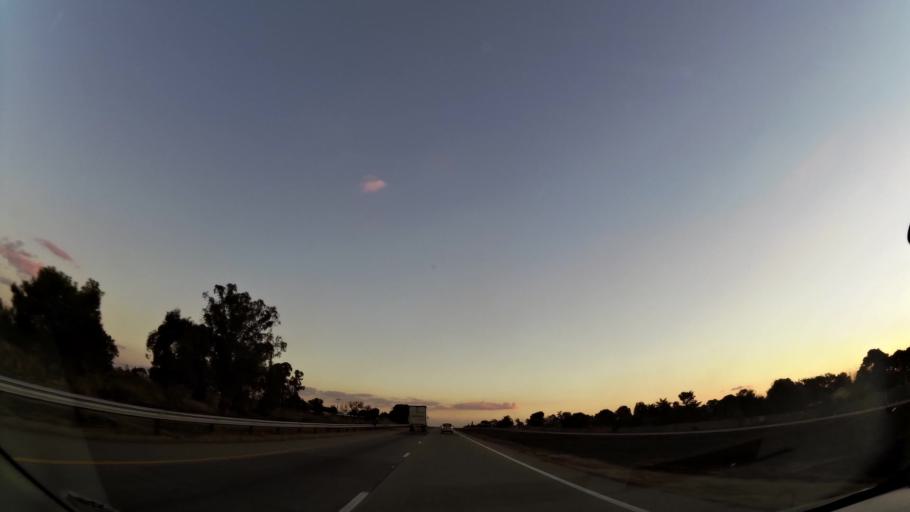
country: ZA
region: Mpumalanga
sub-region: Nkangala District Municipality
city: Witbank
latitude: -25.9006
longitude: 29.2524
